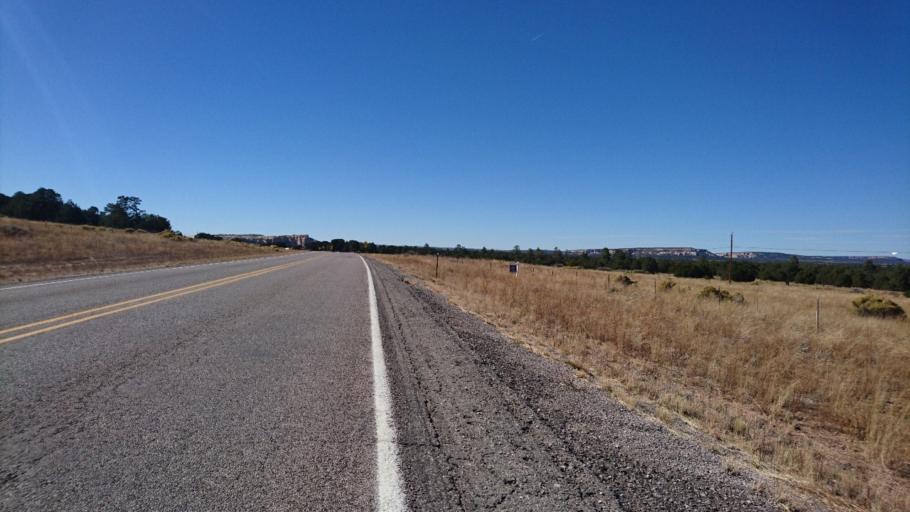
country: US
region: New Mexico
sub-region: McKinley County
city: Thoreau
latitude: 35.0454
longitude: -108.3143
